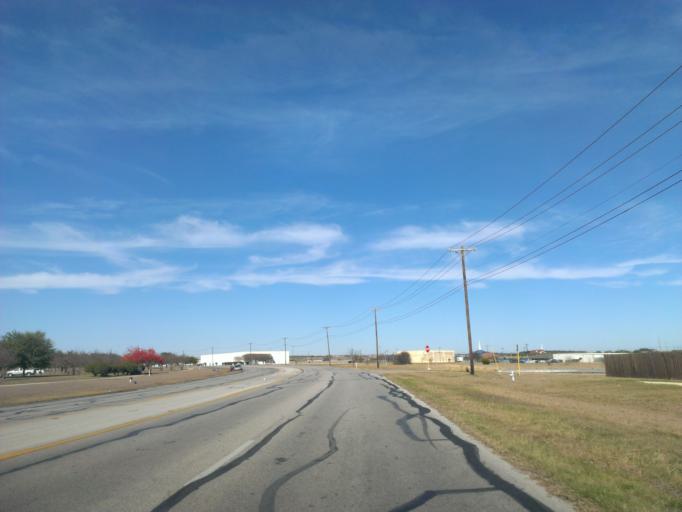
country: US
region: Texas
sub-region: Bell County
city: Harker Heights
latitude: 31.1080
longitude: -97.6836
